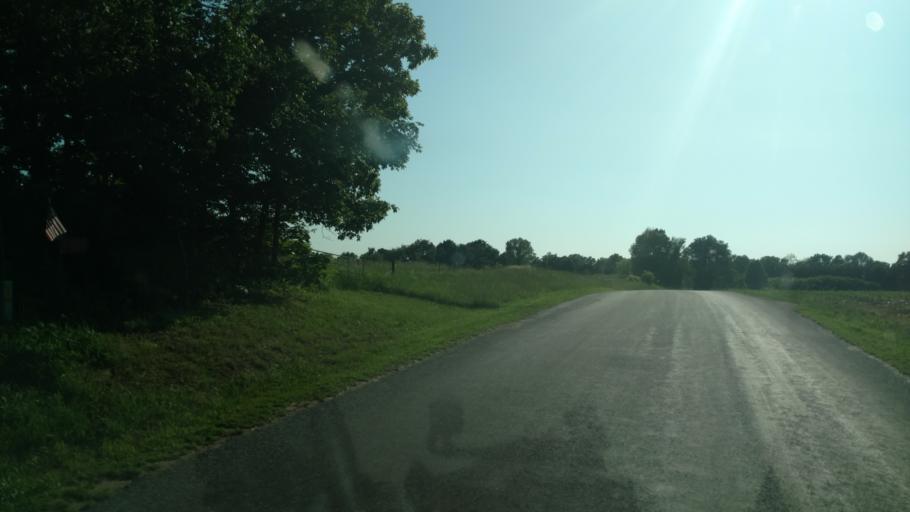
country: US
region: Wisconsin
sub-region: Vernon County
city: Hillsboro
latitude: 43.6755
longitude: -90.3643
